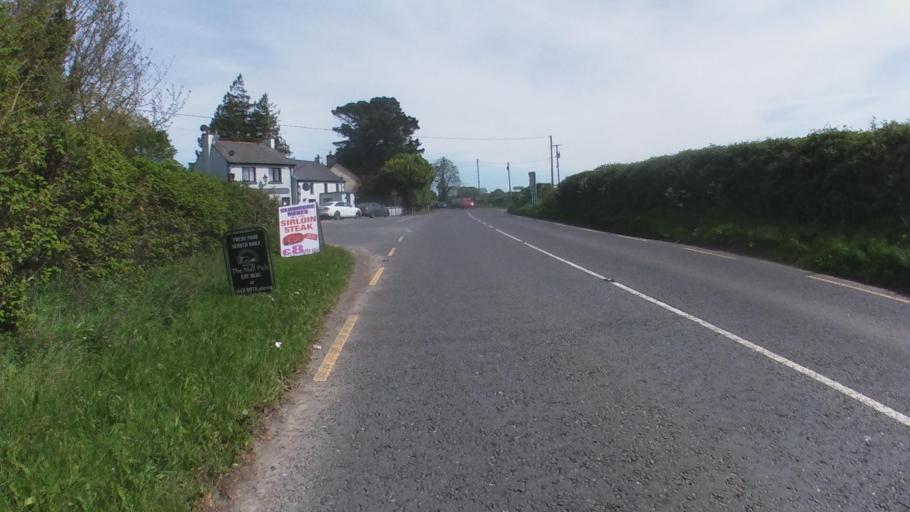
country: IE
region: Leinster
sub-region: County Carlow
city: Carlow
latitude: 52.8430
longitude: -6.9782
